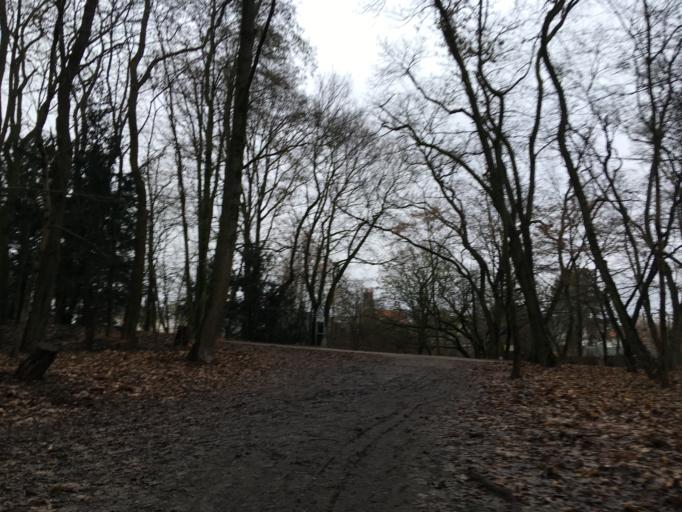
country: DE
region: Berlin
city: Wilhelmsruh
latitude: 52.5789
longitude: 13.3824
